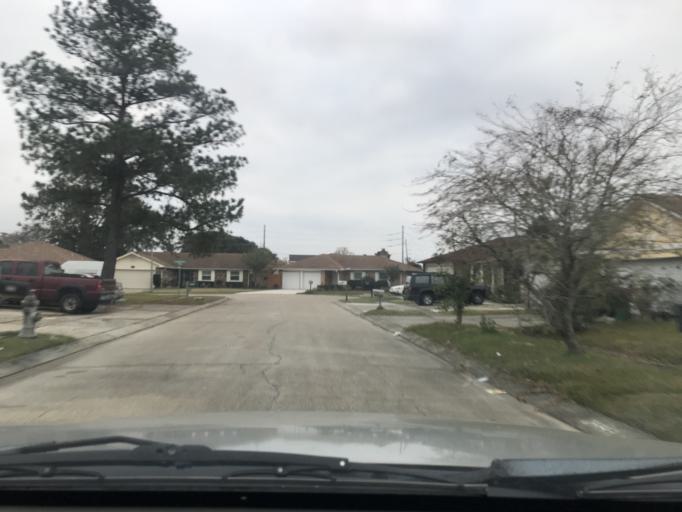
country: US
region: Louisiana
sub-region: Jefferson Parish
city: Woodmere
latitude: 29.8602
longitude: -90.0804
